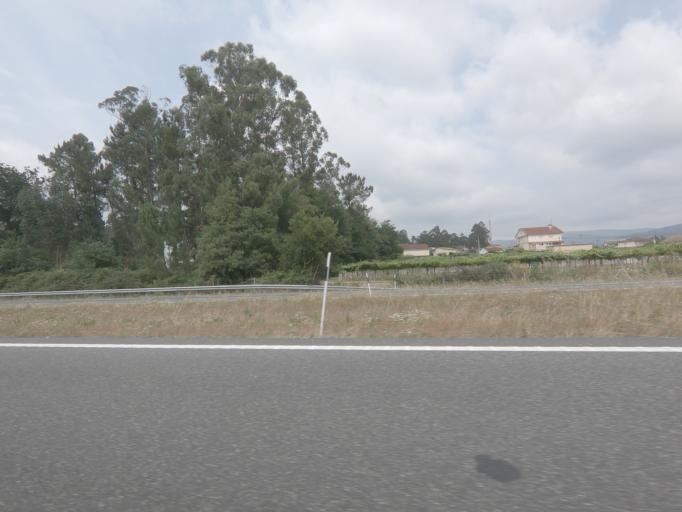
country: ES
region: Galicia
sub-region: Provincia de Pontevedra
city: Ponteareas
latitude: 42.1496
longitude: -8.4781
